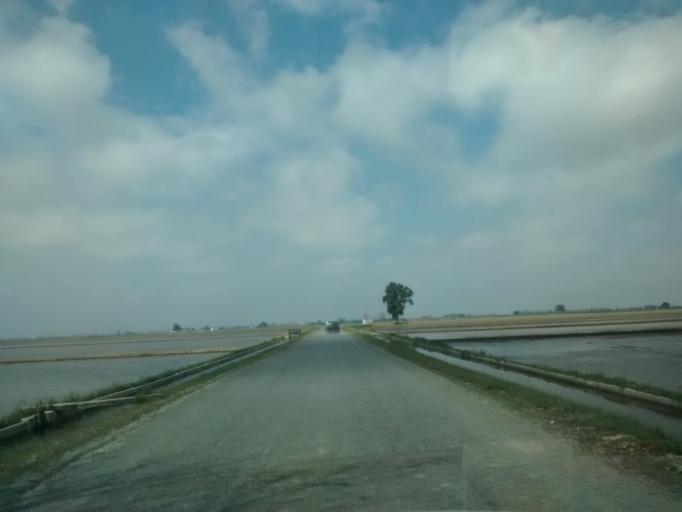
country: ES
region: Catalonia
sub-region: Provincia de Tarragona
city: Deltebre
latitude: 40.6784
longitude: 0.7989
